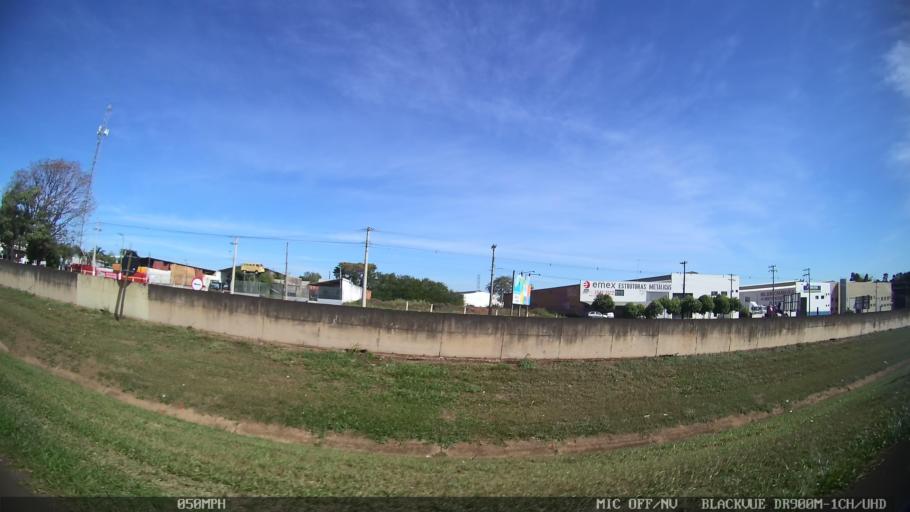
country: BR
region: Sao Paulo
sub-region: Leme
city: Leme
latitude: -22.1741
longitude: -47.3989
